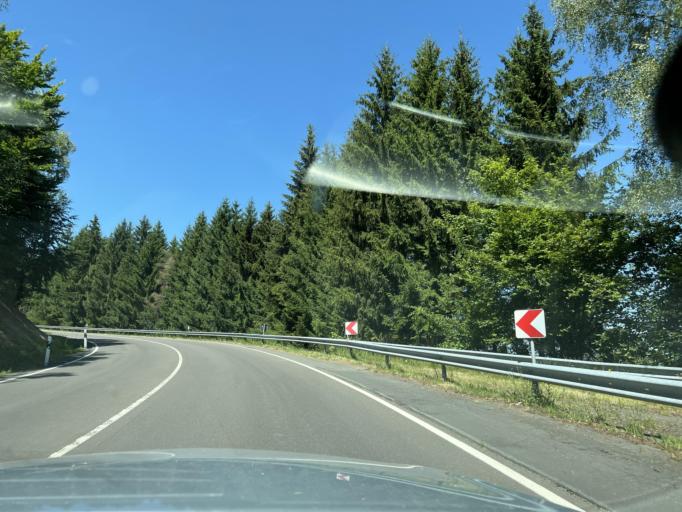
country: DE
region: North Rhine-Westphalia
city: Freudenberg
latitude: 50.9341
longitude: 7.9265
